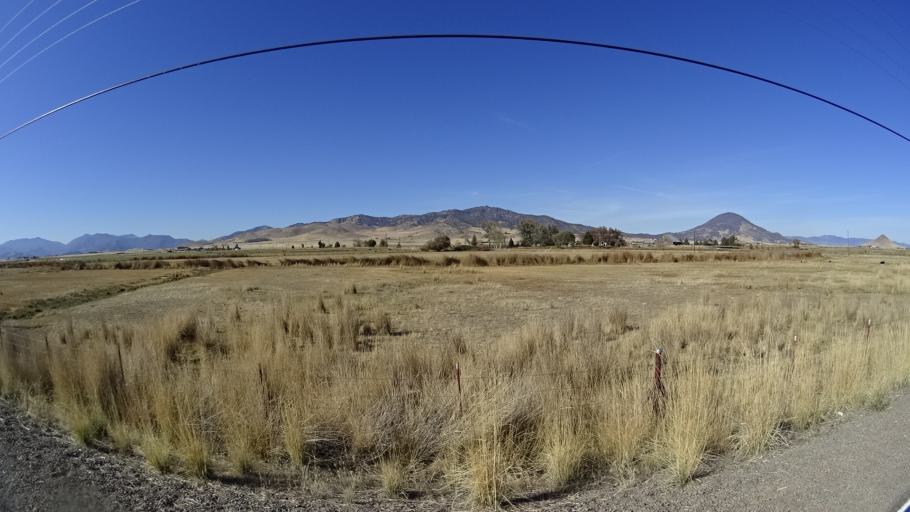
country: US
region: California
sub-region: Siskiyou County
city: Montague
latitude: 41.7688
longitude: -122.4829
